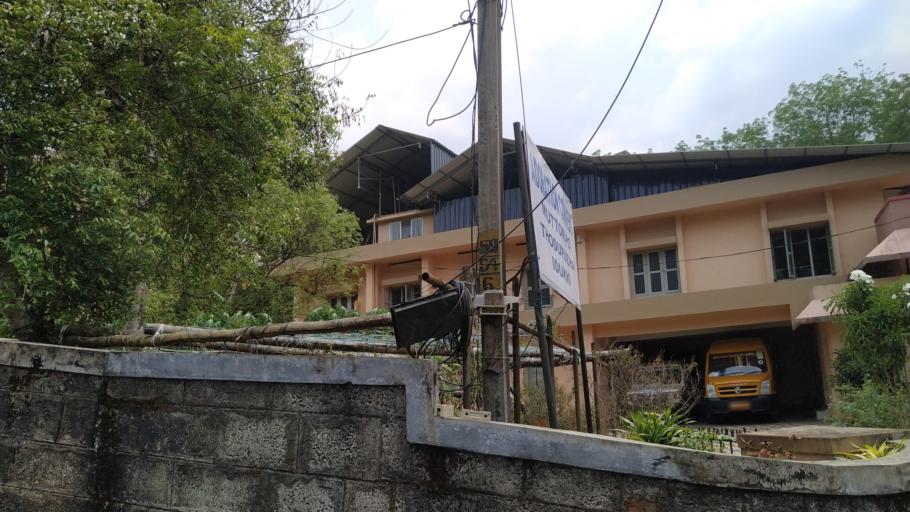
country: IN
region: Kerala
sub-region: Kottayam
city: Lalam
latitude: 9.8398
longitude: 76.7472
